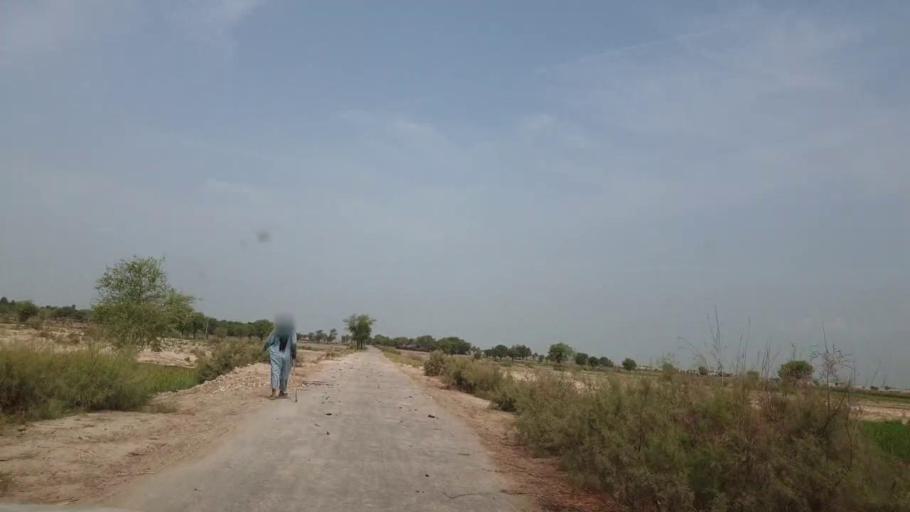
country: PK
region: Sindh
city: Dokri
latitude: 27.4014
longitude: 68.2508
